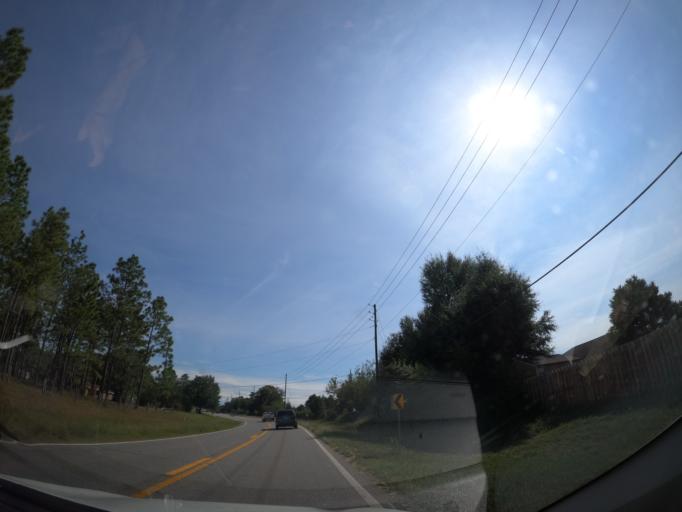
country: US
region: Florida
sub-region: Okaloosa County
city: Crestview
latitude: 30.7204
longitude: -86.6140
